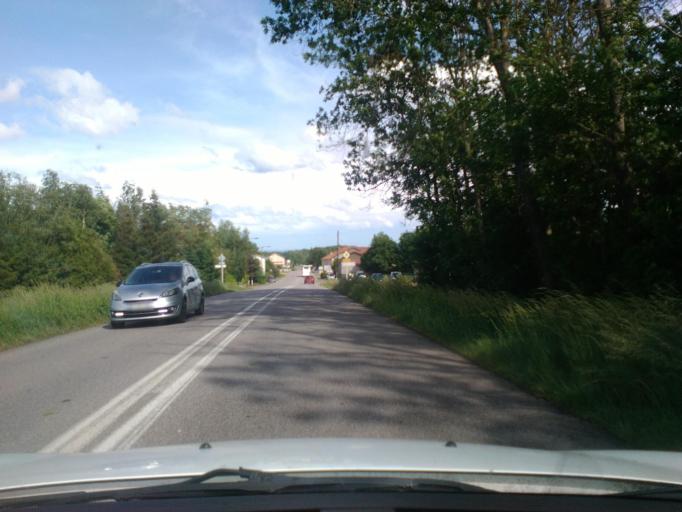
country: FR
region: Lorraine
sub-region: Departement de Meurthe-et-Moselle
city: Baccarat
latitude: 48.5505
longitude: 6.7206
